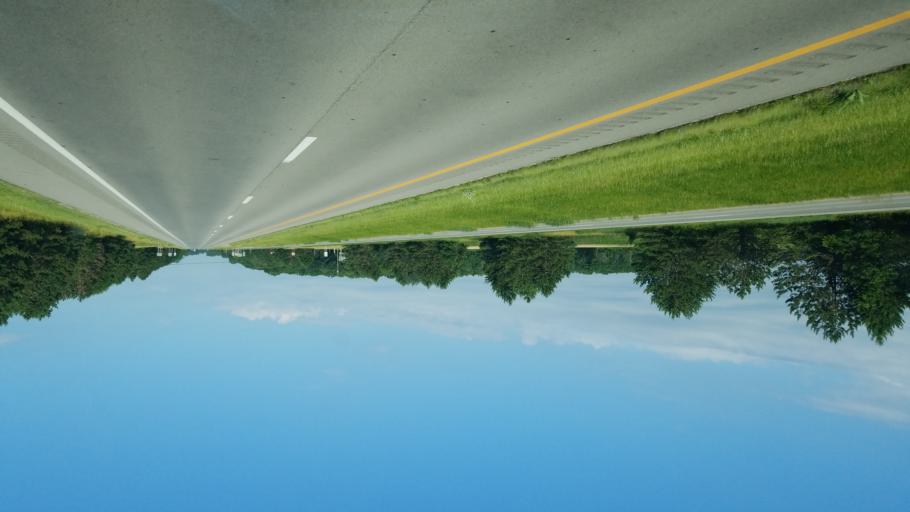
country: US
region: Ohio
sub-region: Wyandot County
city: Carey
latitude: 40.9820
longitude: -83.5099
